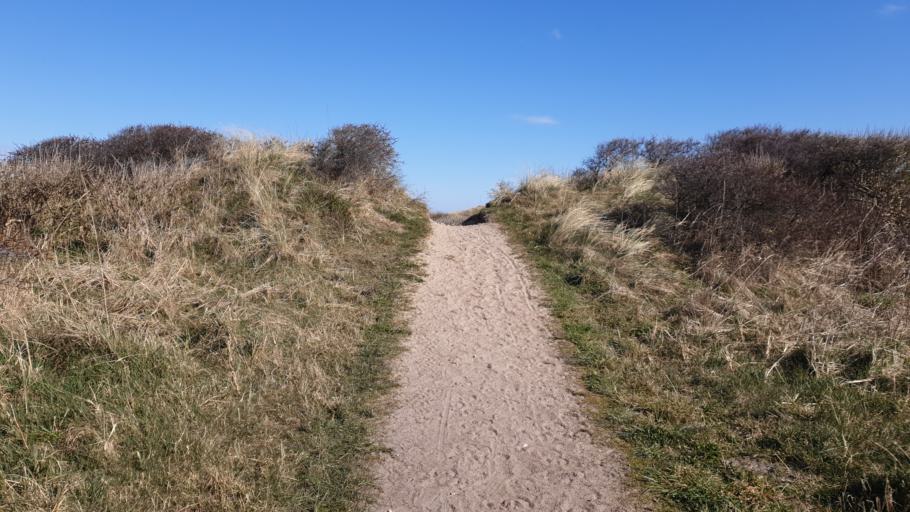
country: DK
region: North Denmark
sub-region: Hjorring Kommune
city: Hjorring
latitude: 57.4949
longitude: 9.8343
